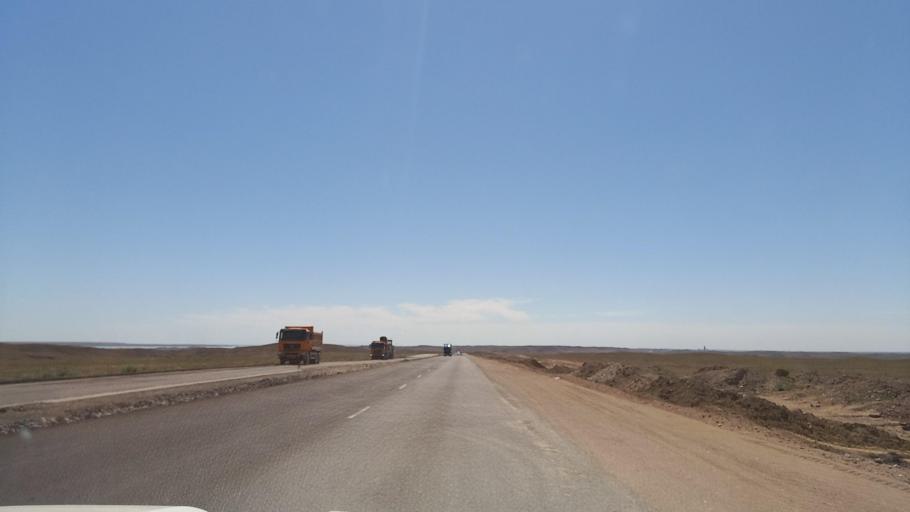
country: KZ
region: Zhambyl
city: Mynaral
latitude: 45.4672
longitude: 73.5648
